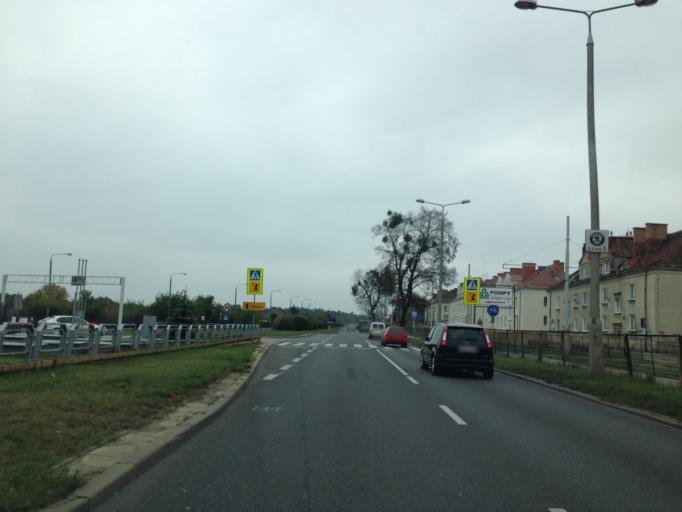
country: PL
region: Kujawsko-Pomorskie
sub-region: Grudziadz
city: Grudziadz
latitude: 53.4638
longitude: 18.7413
